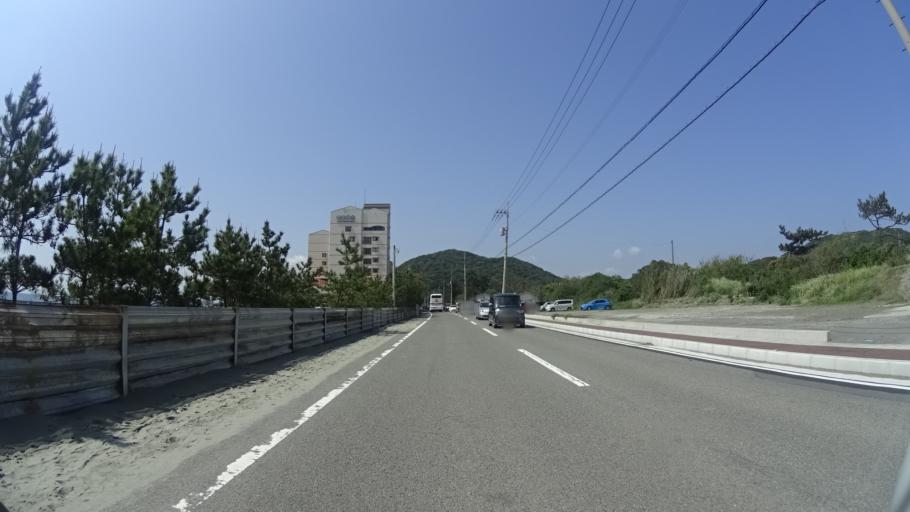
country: JP
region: Tokushima
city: Narutocho-mitsuishi
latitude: 34.2219
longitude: 134.6342
